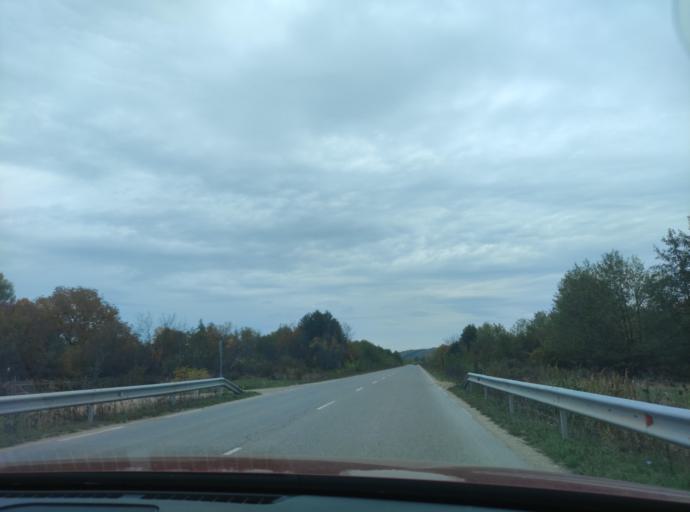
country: BG
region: Montana
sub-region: Obshtina Berkovitsa
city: Berkovitsa
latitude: 43.2364
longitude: 23.1602
